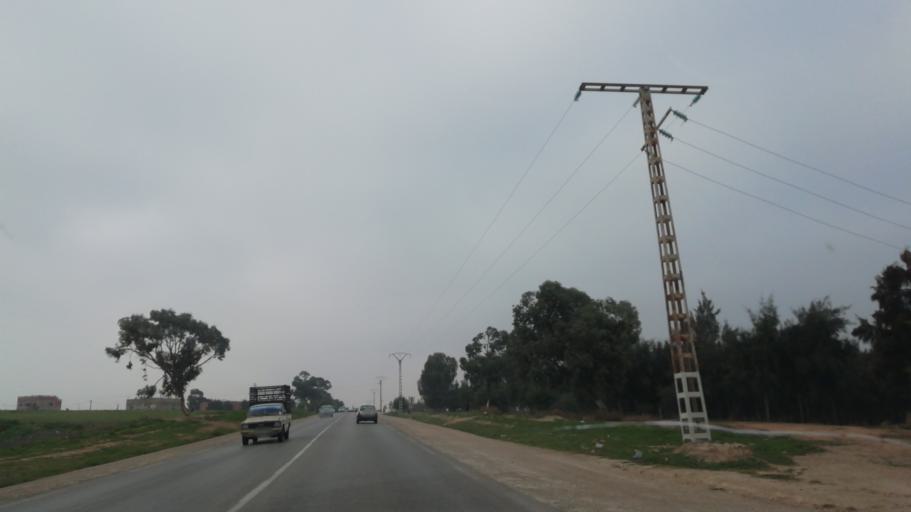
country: DZ
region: Relizane
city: Djidiouia
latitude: 35.8938
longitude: 0.7415
